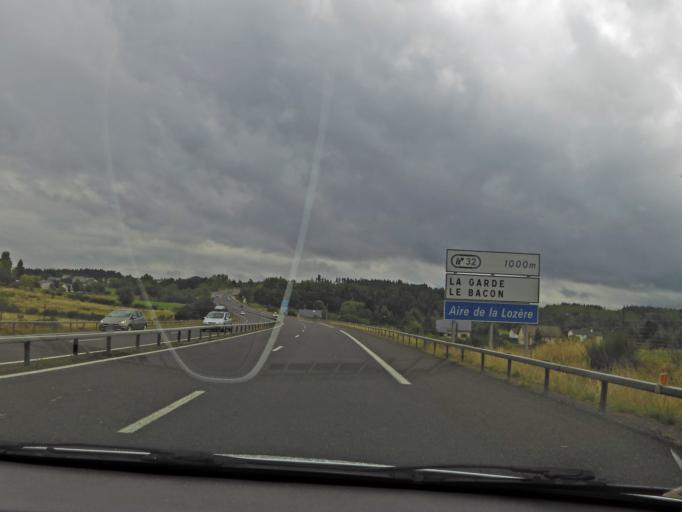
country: FR
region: Languedoc-Roussillon
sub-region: Departement de la Lozere
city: Le Malzieu-Ville
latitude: 44.8833
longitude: 3.2383
